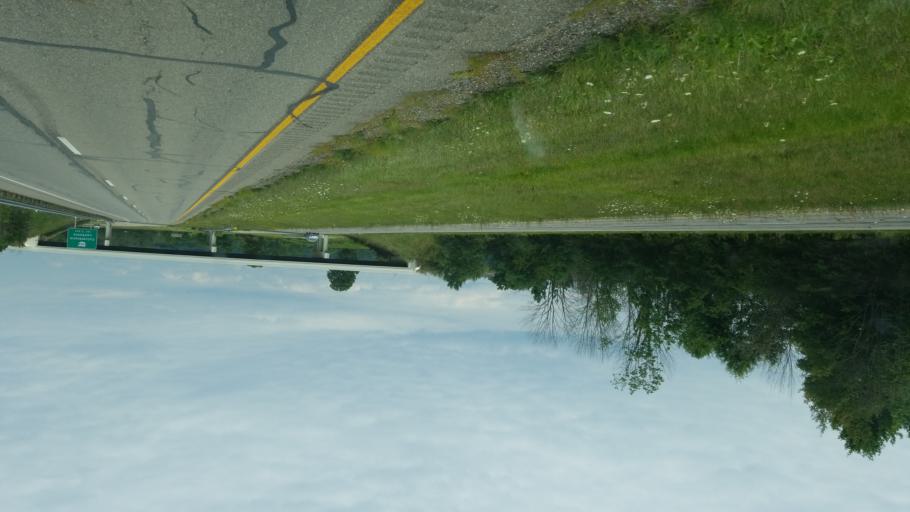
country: US
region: Ohio
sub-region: Columbiana County
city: Leetonia
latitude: 40.8636
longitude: -80.7326
